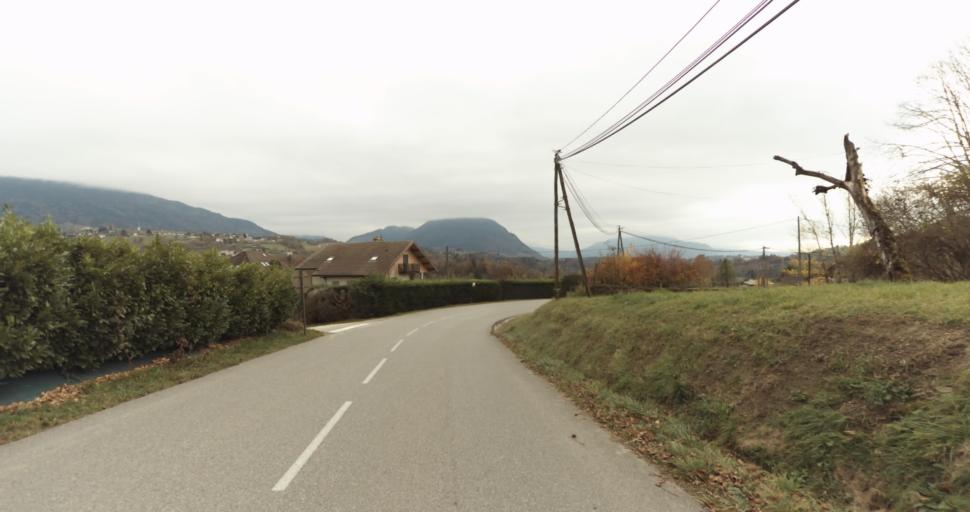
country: FR
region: Rhone-Alpes
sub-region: Departement de la Haute-Savoie
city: Saint-Martin-Bellevue
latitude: 45.9664
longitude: 6.1709
